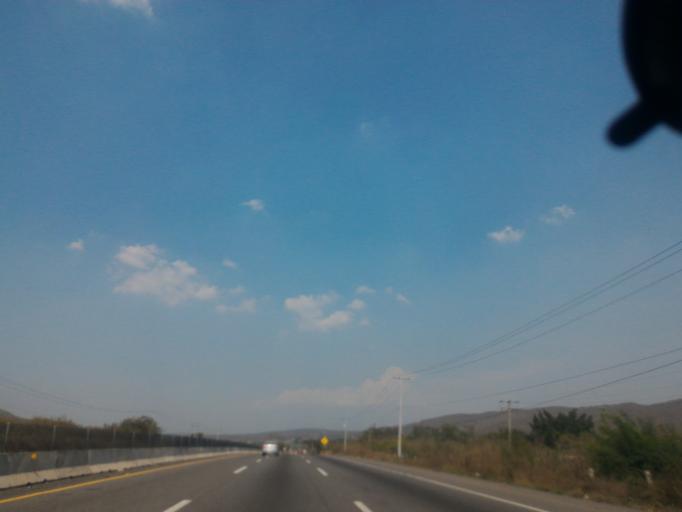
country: MX
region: Colima
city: Coquimatlan
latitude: 19.1349
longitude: -103.7726
